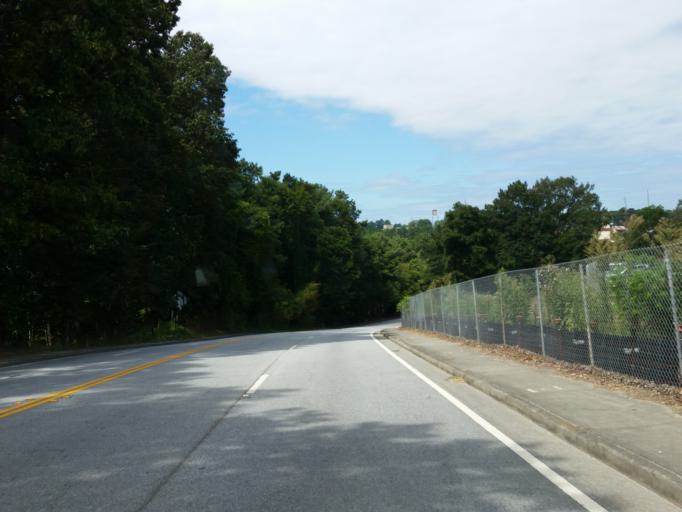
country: US
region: Georgia
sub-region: Cobb County
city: Vinings
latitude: 33.8970
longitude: -84.4713
